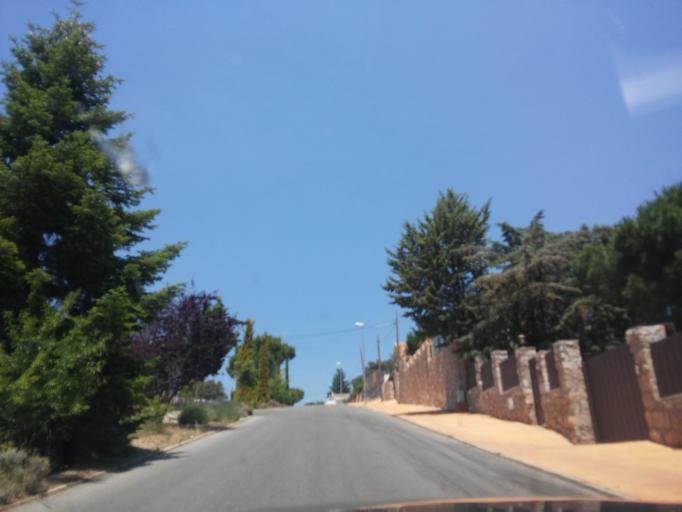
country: ES
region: Madrid
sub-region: Provincia de Madrid
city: Navalquejigo
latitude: 40.6109
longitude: -4.0485
